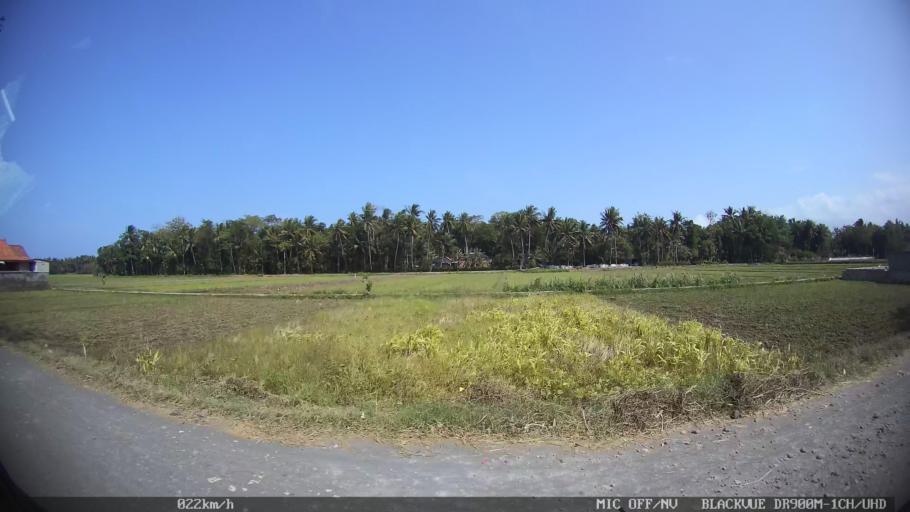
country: ID
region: Daerah Istimewa Yogyakarta
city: Srandakan
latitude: -7.9594
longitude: 110.2157
